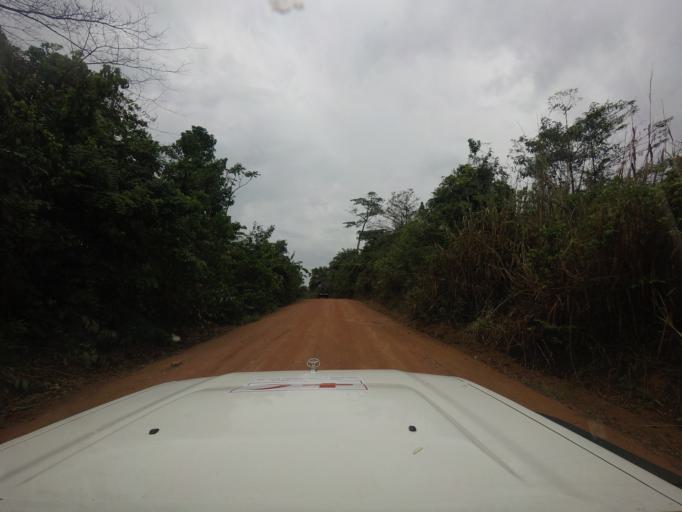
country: SL
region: Eastern Province
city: Buedu
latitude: 8.3110
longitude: -10.1391
